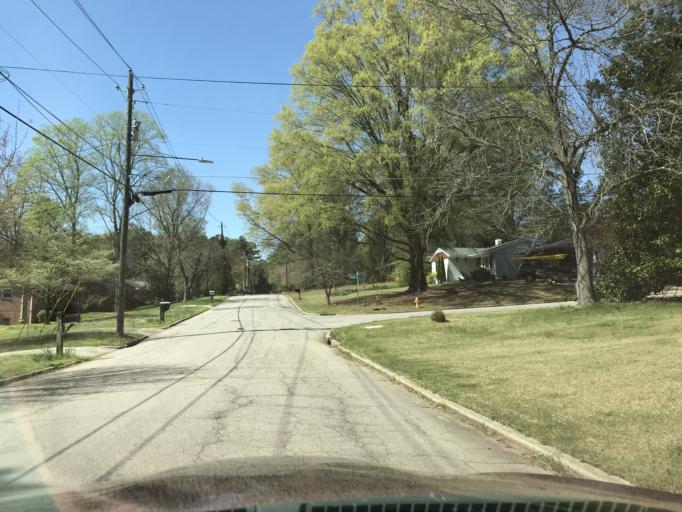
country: US
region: North Carolina
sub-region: Wake County
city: West Raleigh
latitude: 35.7734
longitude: -78.7085
